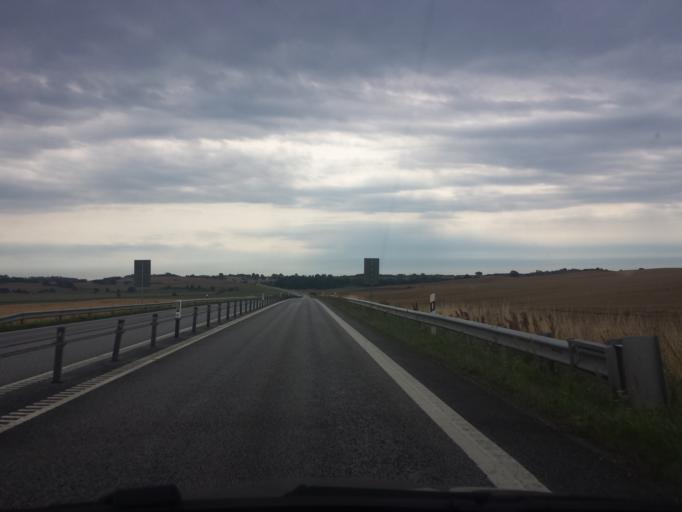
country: SE
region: Skane
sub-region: Ystads Kommun
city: Ystad
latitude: 55.4660
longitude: 13.7138
